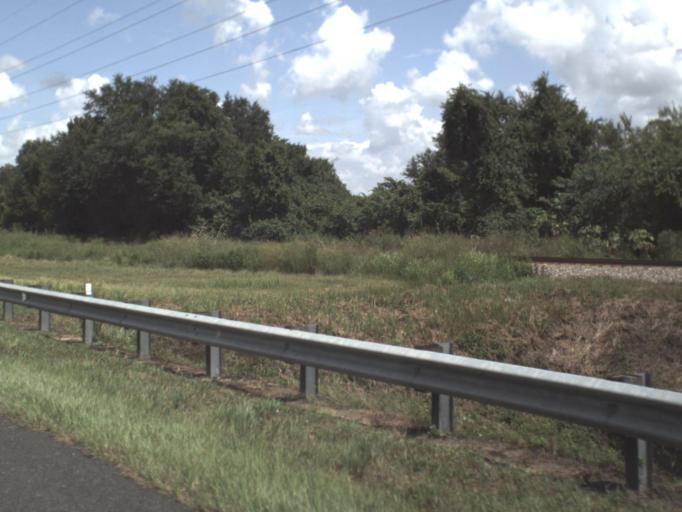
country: US
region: Florida
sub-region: Polk County
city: Bartow
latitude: 27.8348
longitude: -81.8233
